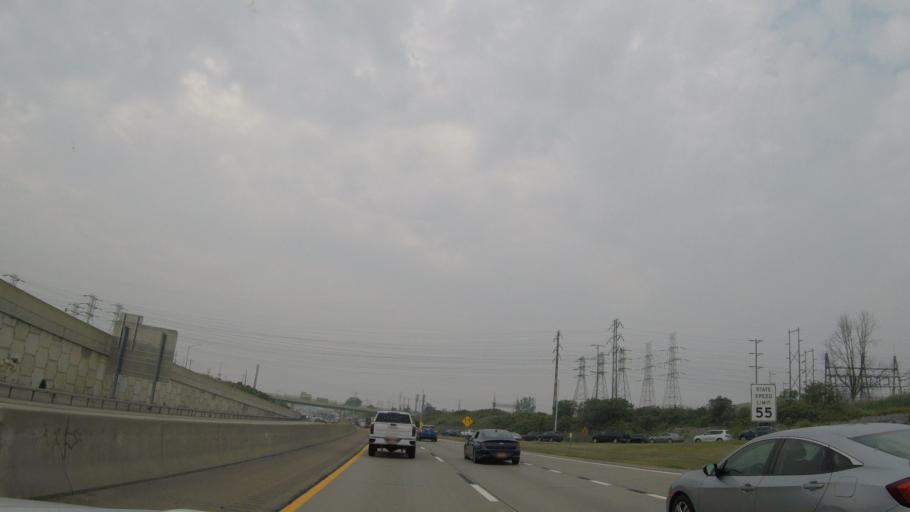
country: US
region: New York
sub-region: Erie County
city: Tonawanda
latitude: 42.9877
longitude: -78.9156
